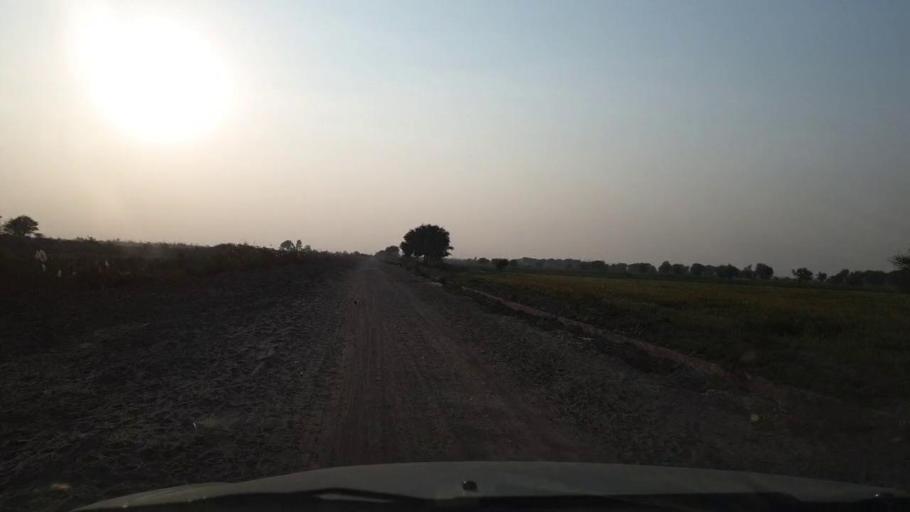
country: PK
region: Sindh
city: Pithoro
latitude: 25.6532
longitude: 69.2070
